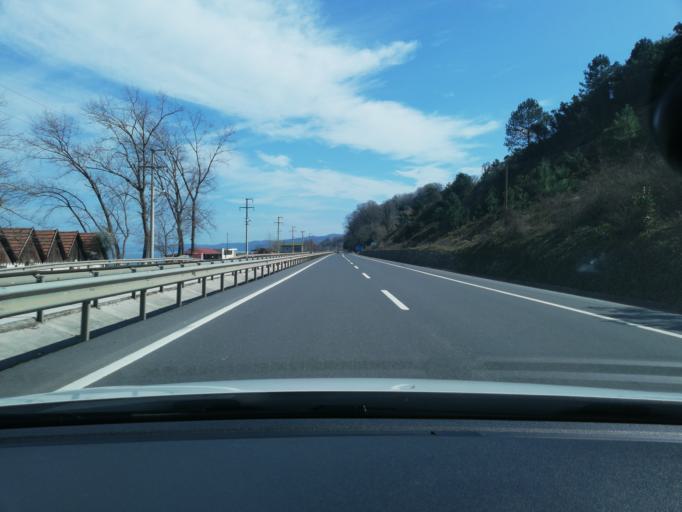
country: TR
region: Duzce
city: Akcakoca
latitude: 41.0957
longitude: 31.2019
